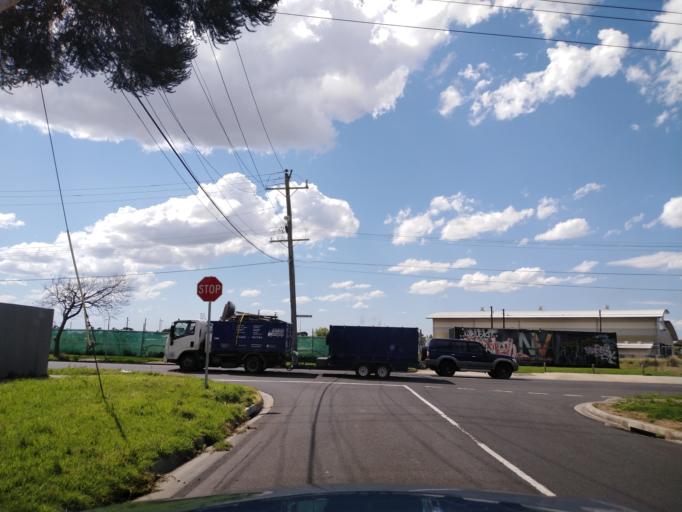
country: AU
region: Victoria
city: Spotswood
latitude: -37.8347
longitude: 144.8789
